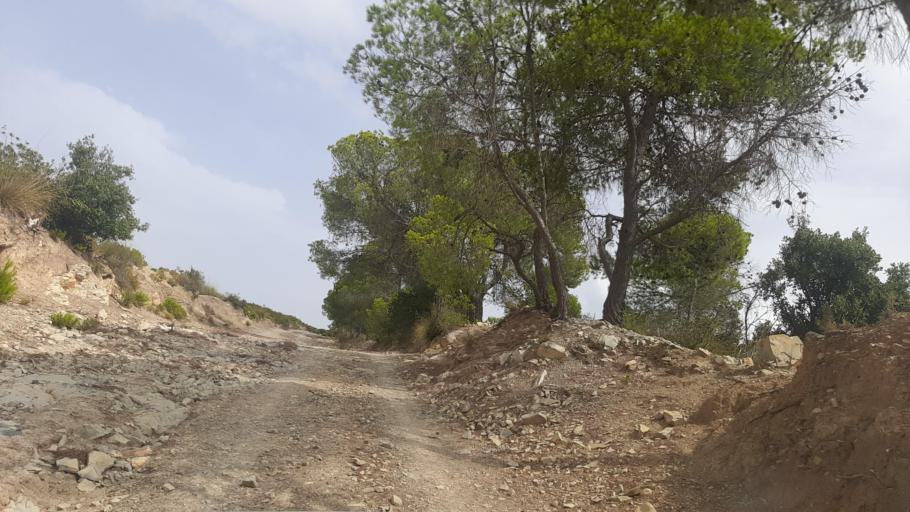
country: TN
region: Zaghwan
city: El Fahs
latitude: 36.1962
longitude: 9.8503
